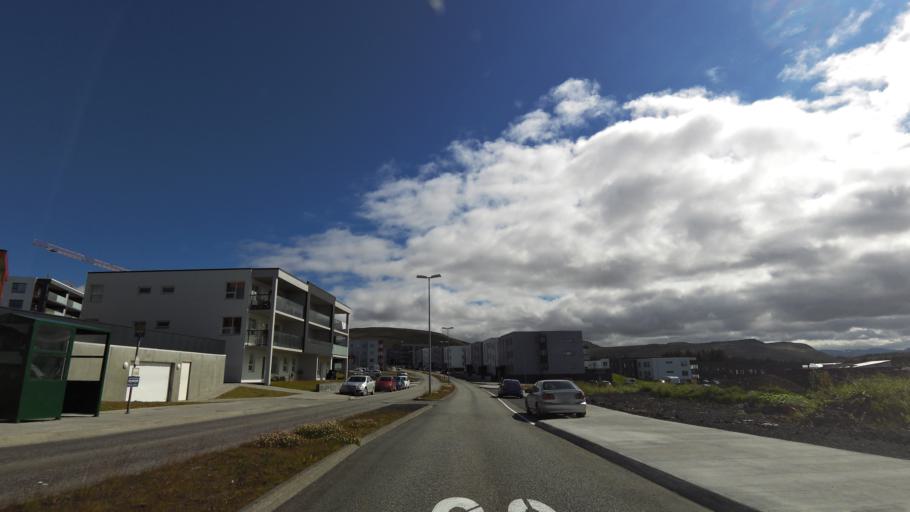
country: IS
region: Capital Region
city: Mosfellsbaer
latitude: 64.1690
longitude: -21.6719
